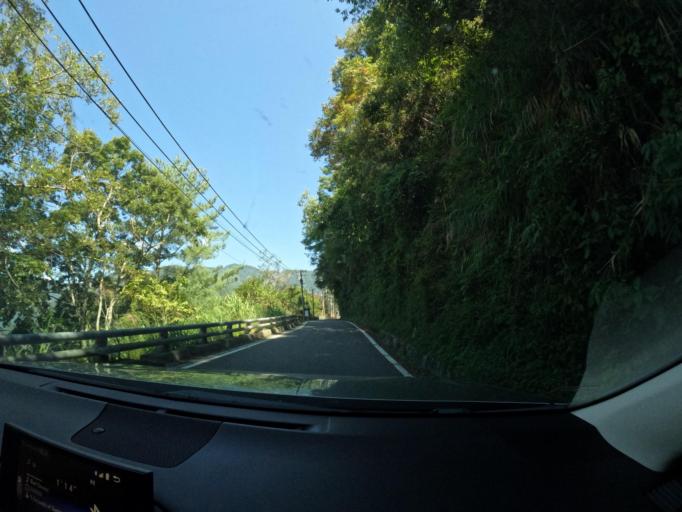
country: TW
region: Taiwan
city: Yujing
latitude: 23.2832
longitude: 120.8708
